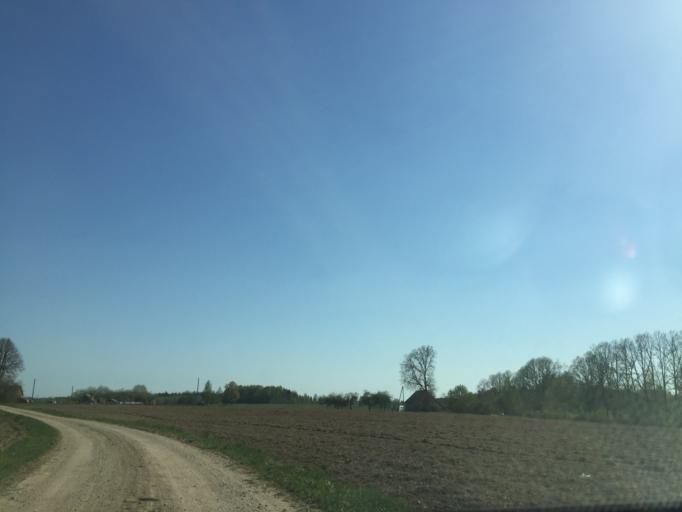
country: LV
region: Malpils
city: Malpils
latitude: 56.9334
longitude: 24.9247
